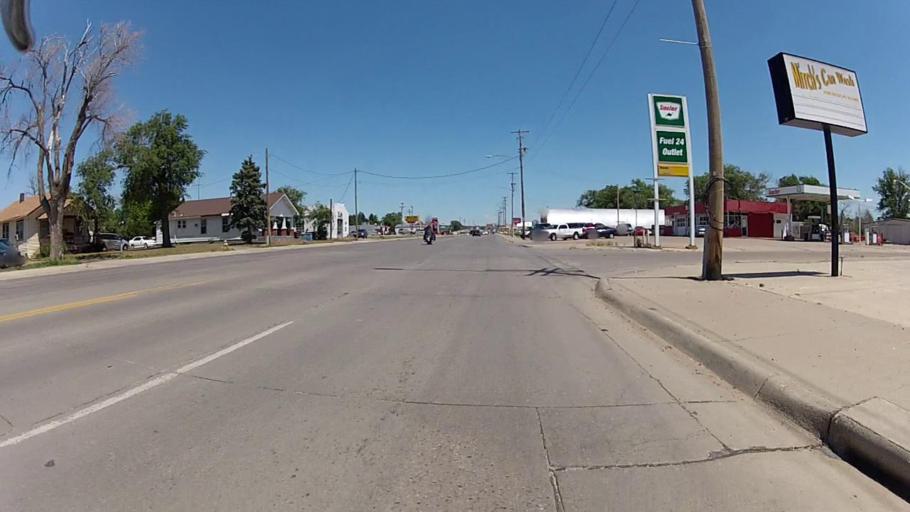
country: US
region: Kansas
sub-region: Ford County
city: Dodge City
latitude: 37.7379
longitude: -100.0194
